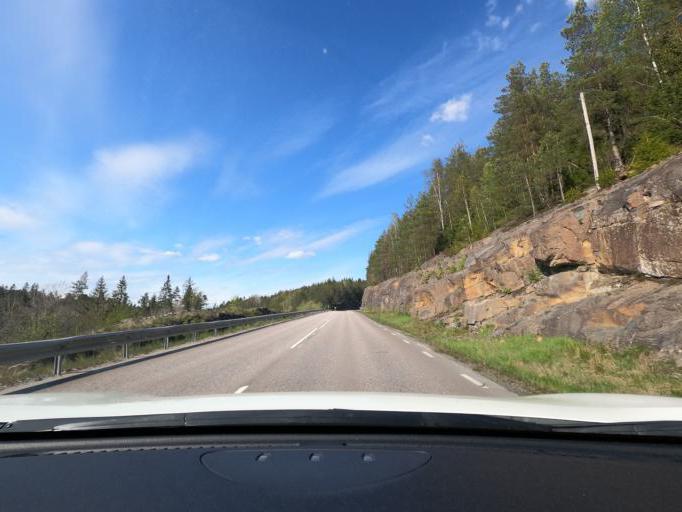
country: SE
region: Vaestra Goetaland
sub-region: Harryda Kommun
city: Ravlanda
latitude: 57.6669
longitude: 12.4868
